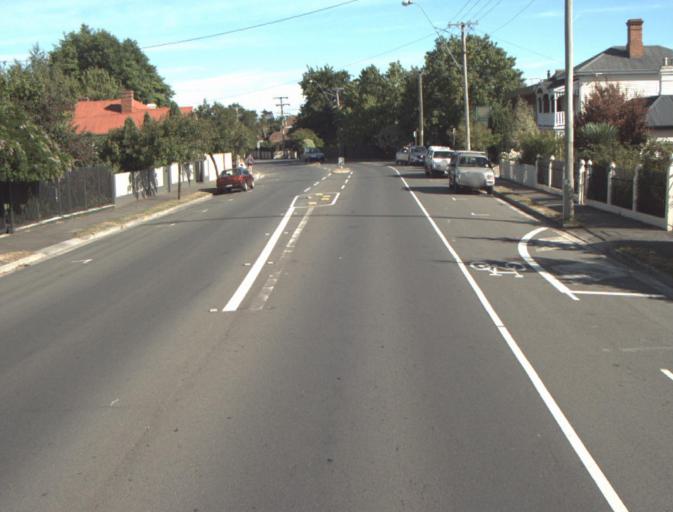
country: AU
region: Tasmania
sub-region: Launceston
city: East Launceston
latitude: -41.4366
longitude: 147.1572
